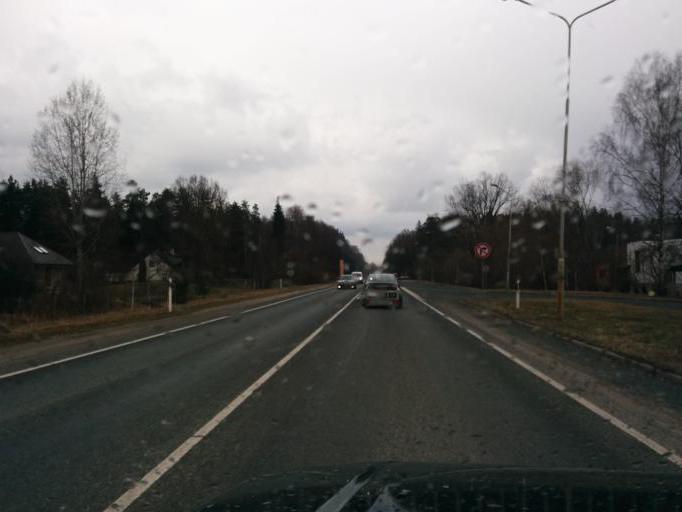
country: LV
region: Ozolnieku
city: Ozolnieki
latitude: 56.6946
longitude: 23.8019
